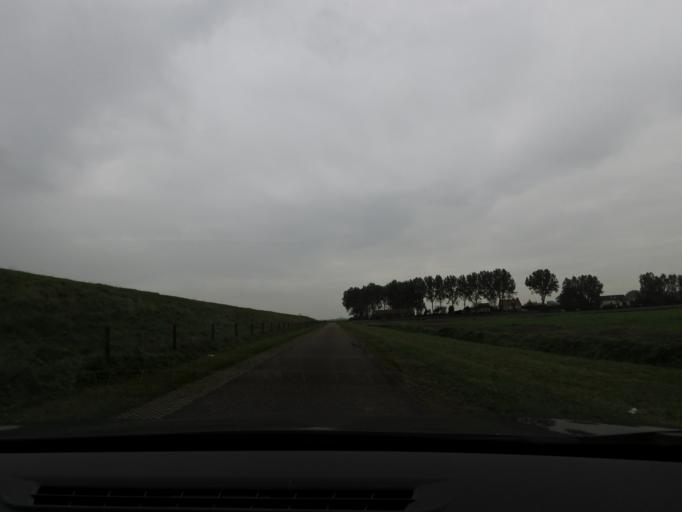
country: NL
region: South Holland
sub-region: Gemeente Goeree-Overflakkee
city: Middelharnis
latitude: 51.8083
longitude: 4.1986
